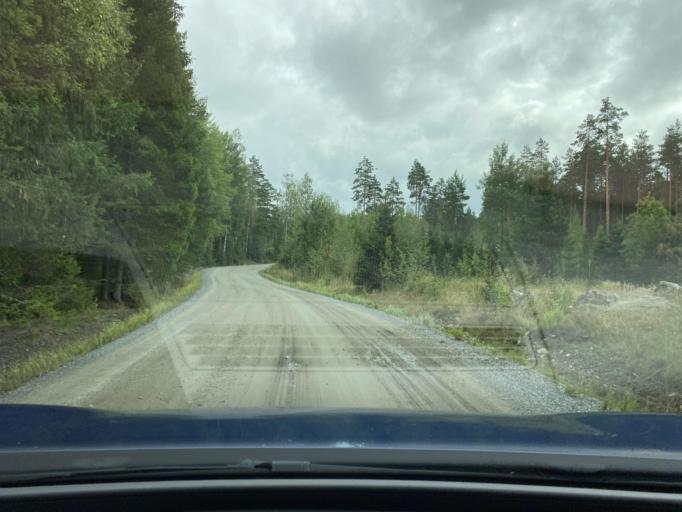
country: FI
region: Pirkanmaa
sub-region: Lounais-Pirkanmaa
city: Vammala
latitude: 61.2561
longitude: 23.0179
